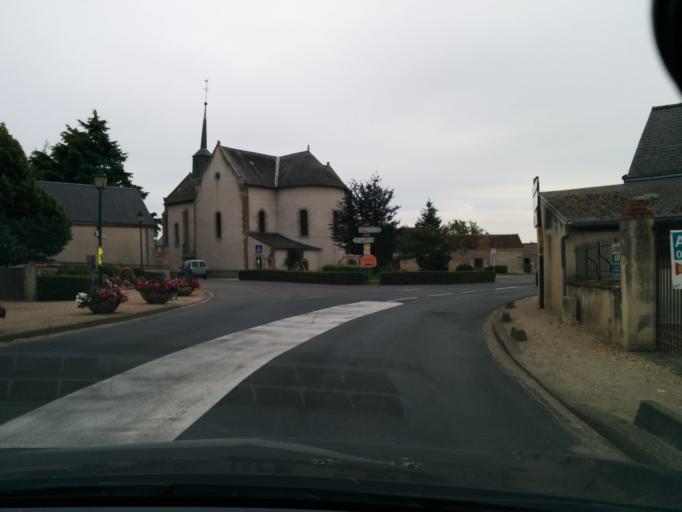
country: FR
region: Centre
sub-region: Departement du Loiret
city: Chateauneuf-sur-Loire
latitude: 47.8342
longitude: 2.2252
